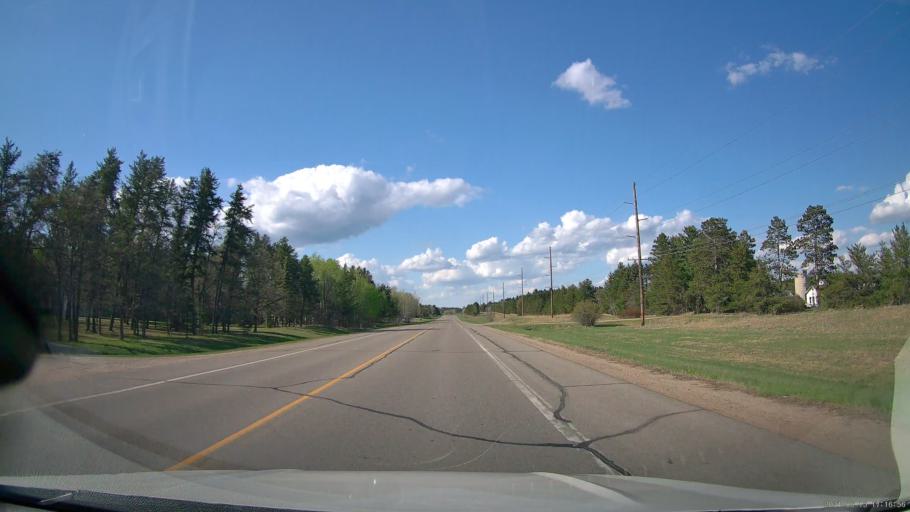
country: US
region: Minnesota
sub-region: Hubbard County
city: Park Rapids
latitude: 46.9365
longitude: -95.0168
